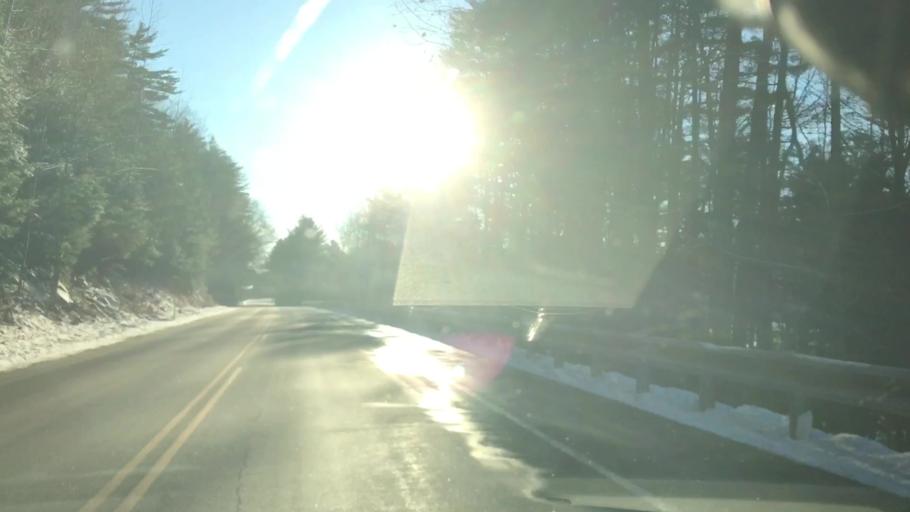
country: US
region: New Hampshire
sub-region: Grafton County
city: Orford
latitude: 43.9517
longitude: -72.1009
